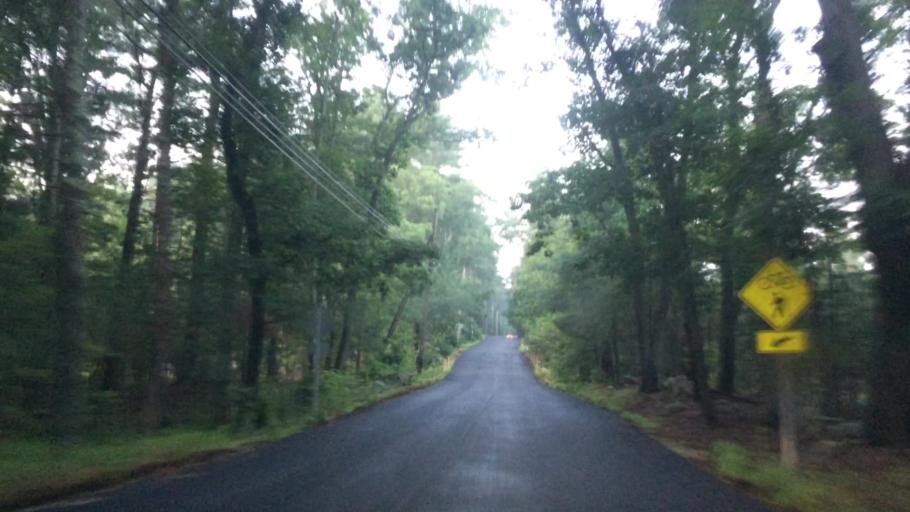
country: US
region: Massachusetts
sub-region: Middlesex County
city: North Reading
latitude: 42.6187
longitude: -71.0936
